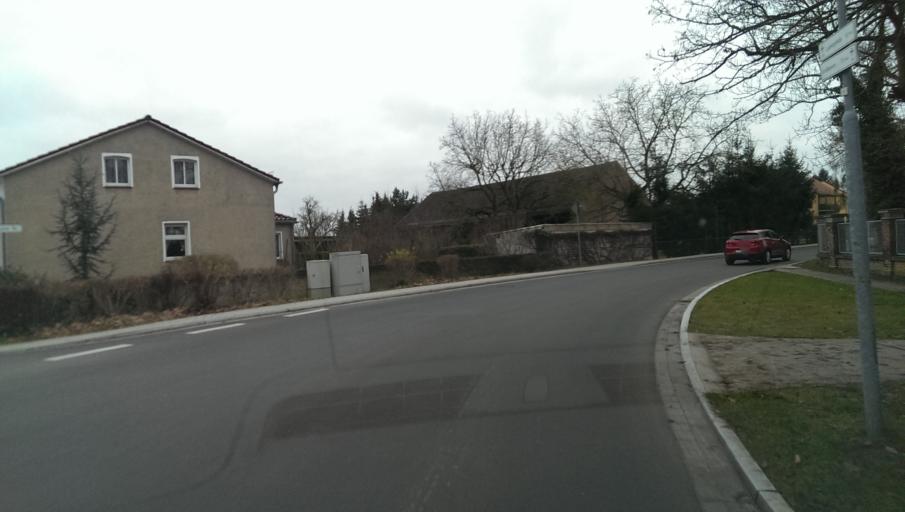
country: DE
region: Brandenburg
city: Grossbeeren
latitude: 52.3142
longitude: 13.3169
